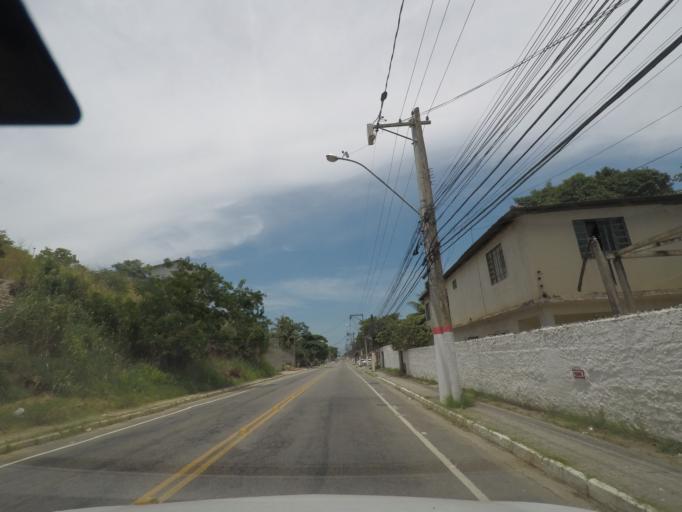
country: BR
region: Rio de Janeiro
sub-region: Marica
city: Marica
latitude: -22.9357
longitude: -42.8270
